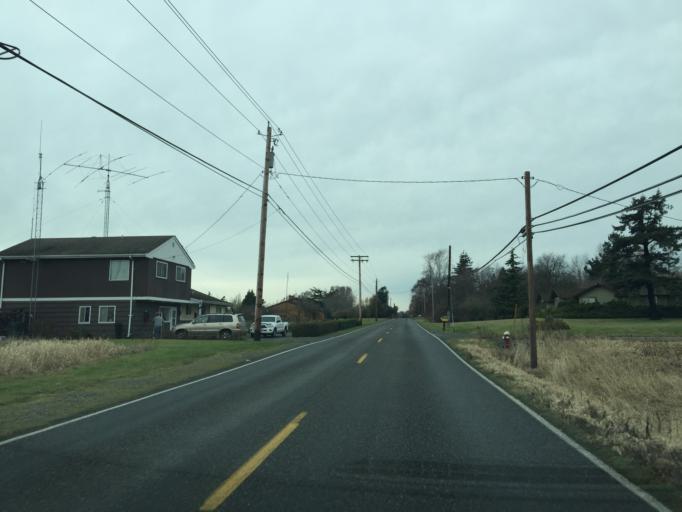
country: US
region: Washington
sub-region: Whatcom County
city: Marietta-Alderwood
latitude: 48.7763
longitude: -122.5340
